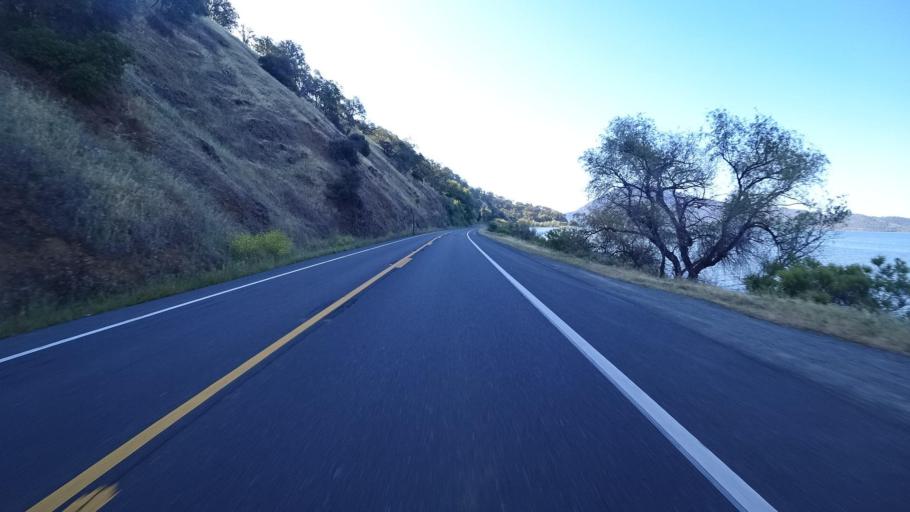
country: US
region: California
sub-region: Lake County
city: Lucerne
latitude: 39.0537
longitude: -122.7822
